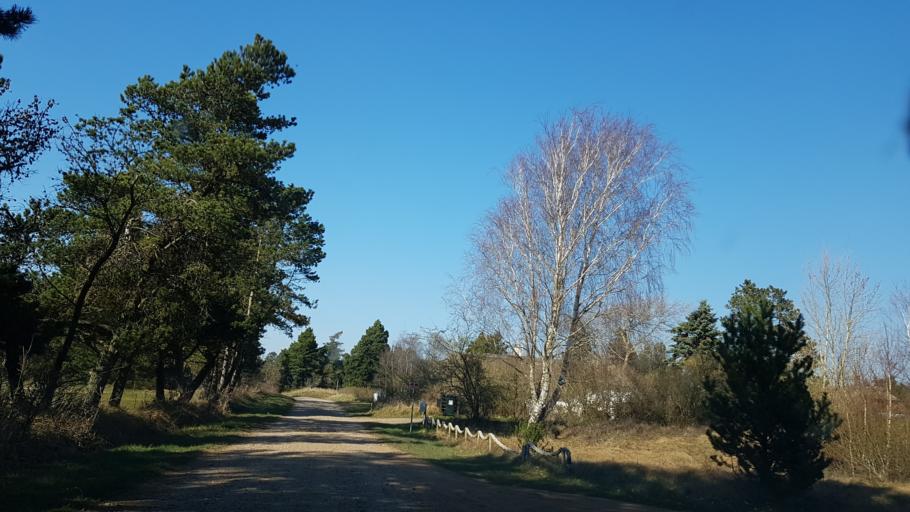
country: DE
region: Schleswig-Holstein
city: List
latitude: 55.0997
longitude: 8.5346
